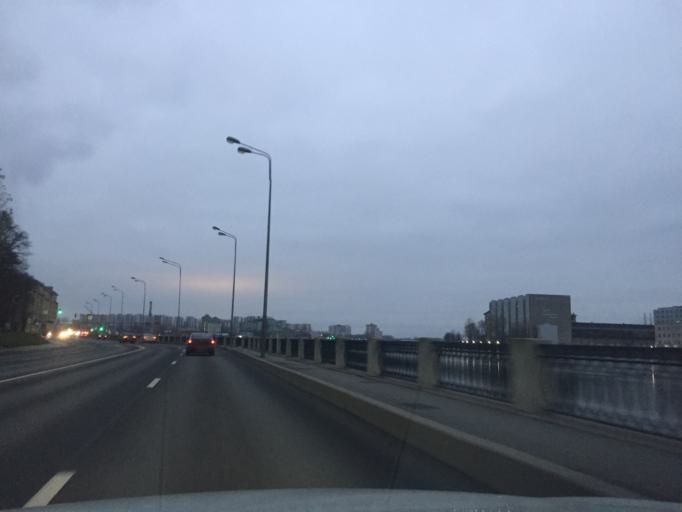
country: RU
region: St.-Petersburg
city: Obukhovo
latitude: 59.8710
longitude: 30.4688
